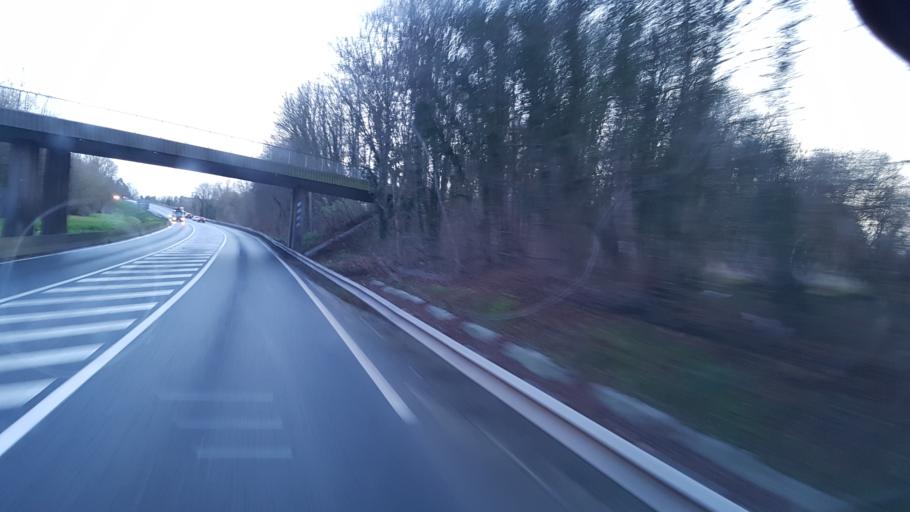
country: FR
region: Nord-Pas-de-Calais
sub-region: Departement du Nord
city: Lauwin-Planque
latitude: 50.3815
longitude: 3.0267
